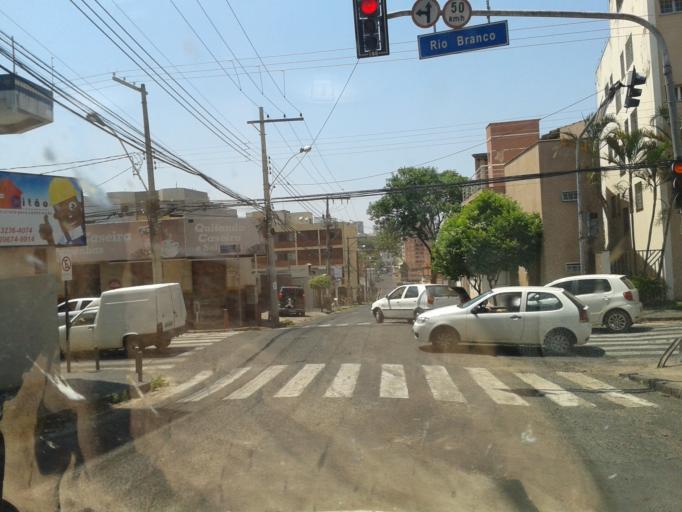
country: BR
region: Minas Gerais
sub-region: Uberlandia
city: Uberlandia
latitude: -18.9173
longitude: -48.2692
